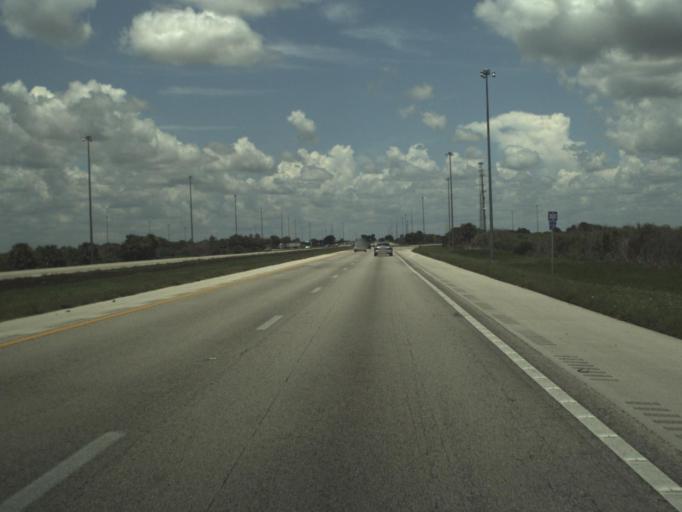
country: US
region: Florida
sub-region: Broward County
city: Weston
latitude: 26.1466
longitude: -80.6192
